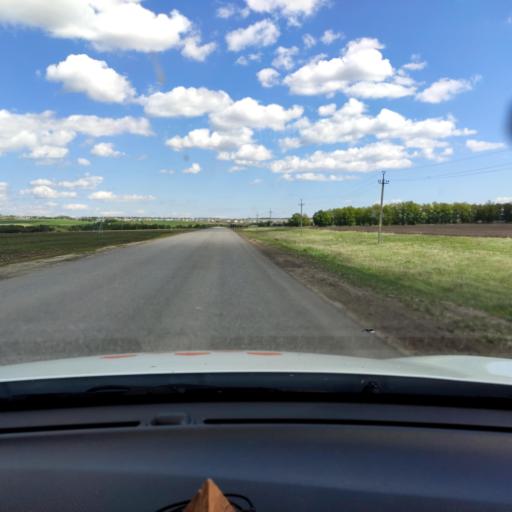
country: RU
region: Tatarstan
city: Kuybyshevskiy Zaton
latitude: 55.1688
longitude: 49.2125
